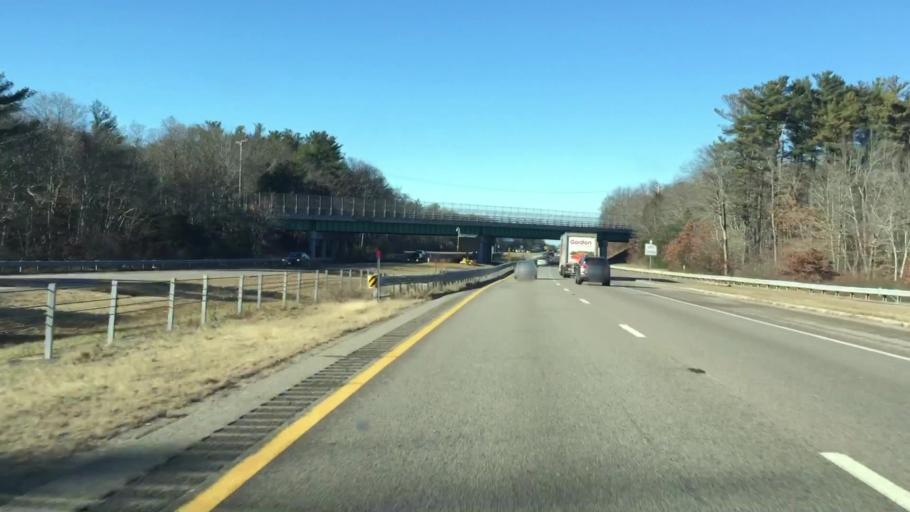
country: US
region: Massachusetts
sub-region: Plymouth County
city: Middleborough Center
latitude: 41.8977
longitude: -70.9570
